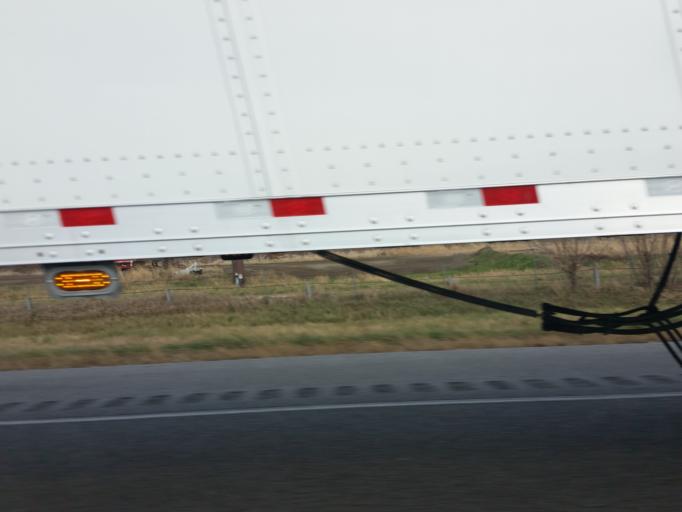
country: US
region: Illinois
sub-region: Henry County
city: Green Rock
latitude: 41.4619
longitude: -90.3840
